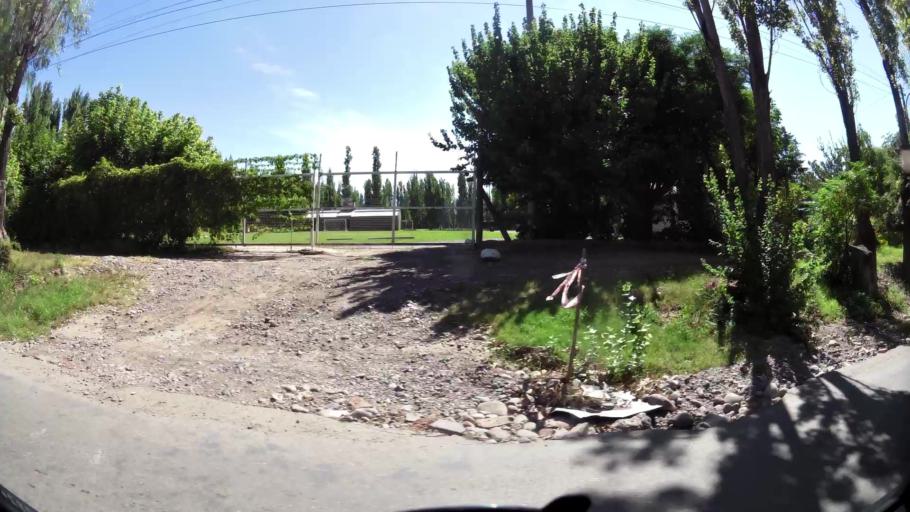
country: AR
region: Mendoza
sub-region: Departamento de Godoy Cruz
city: Godoy Cruz
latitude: -32.9784
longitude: -68.8418
